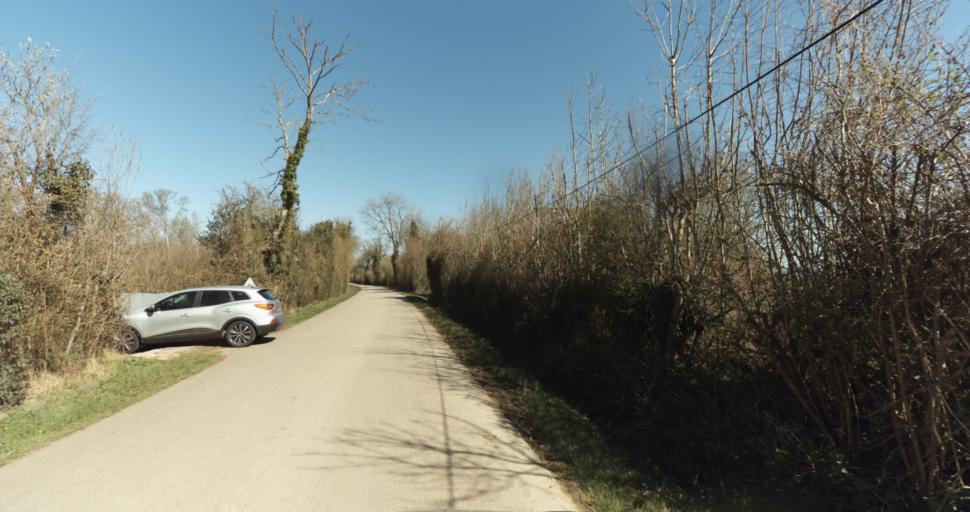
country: FR
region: Lower Normandy
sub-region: Departement de l'Orne
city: Trun
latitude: 48.9153
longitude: 0.0629
